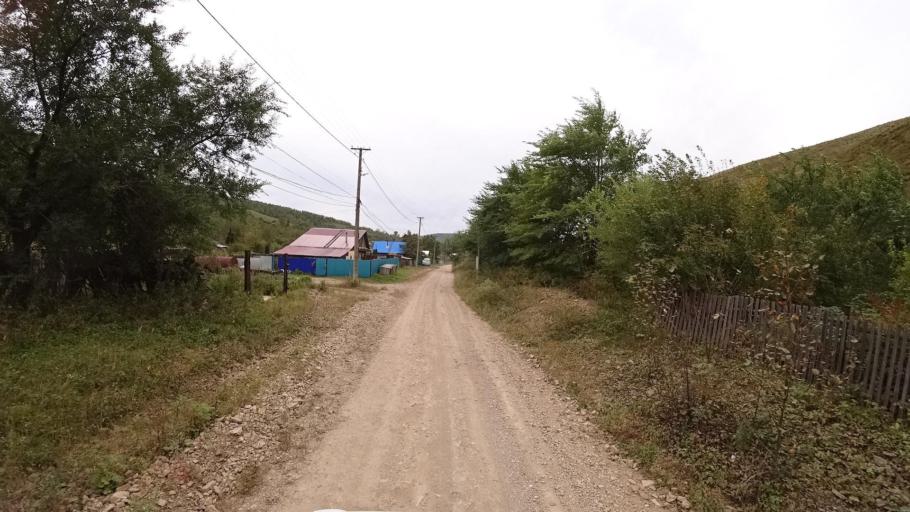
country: RU
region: Jewish Autonomous Oblast
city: Khingansk
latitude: 49.0248
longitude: 131.0720
